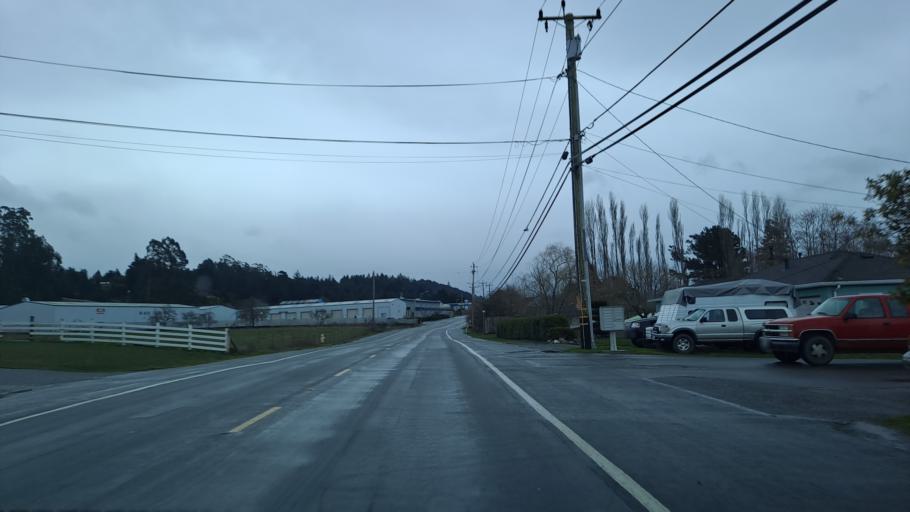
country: US
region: California
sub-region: Humboldt County
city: Fortuna
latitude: 40.5858
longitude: -124.1319
